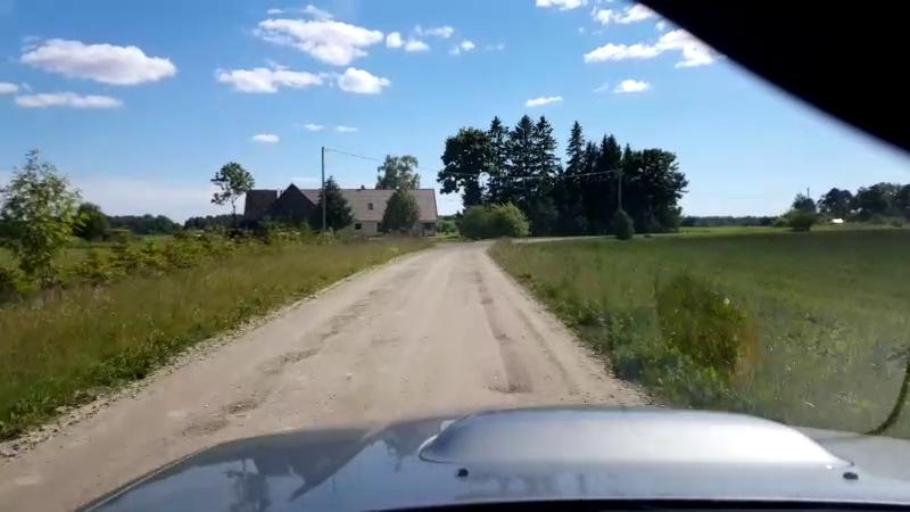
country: EE
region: Paernumaa
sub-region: Sauga vald
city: Sauga
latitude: 58.5170
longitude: 24.5189
